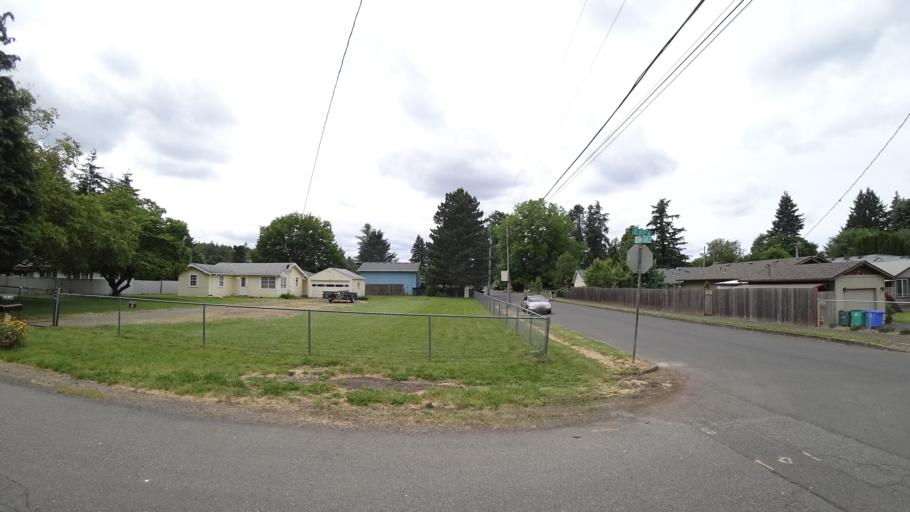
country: US
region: Oregon
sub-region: Multnomah County
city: Lents
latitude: 45.5026
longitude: -122.5575
